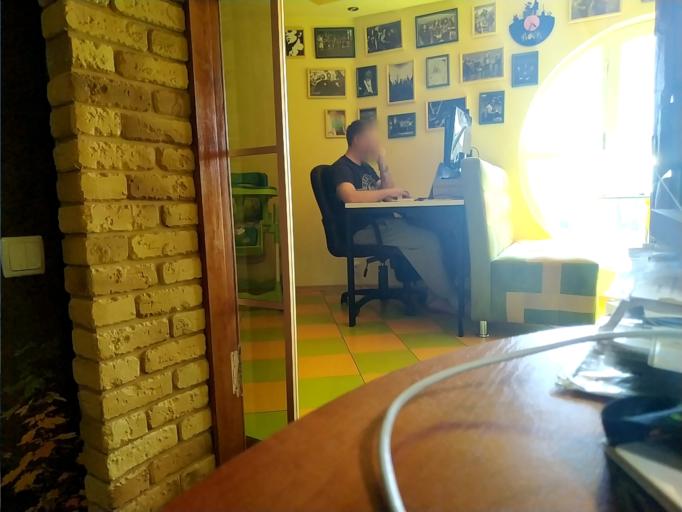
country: RU
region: Moskovskaya
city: Rakhmanovo
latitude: 55.7372
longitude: 38.5752
